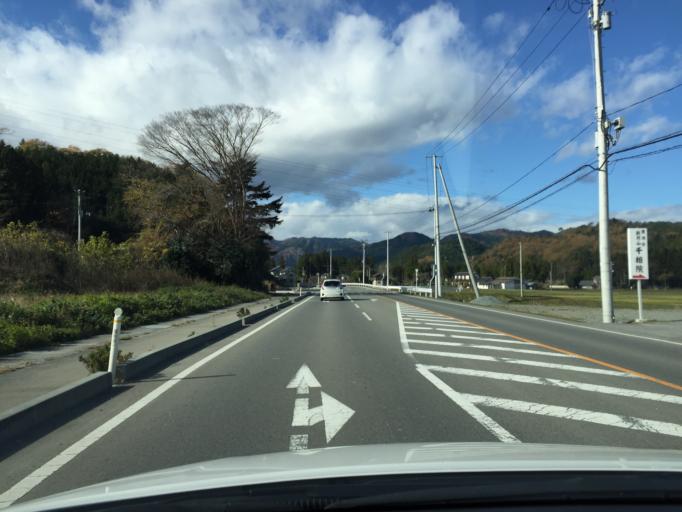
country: JP
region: Fukushima
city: Namie
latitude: 37.6614
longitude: 140.9180
